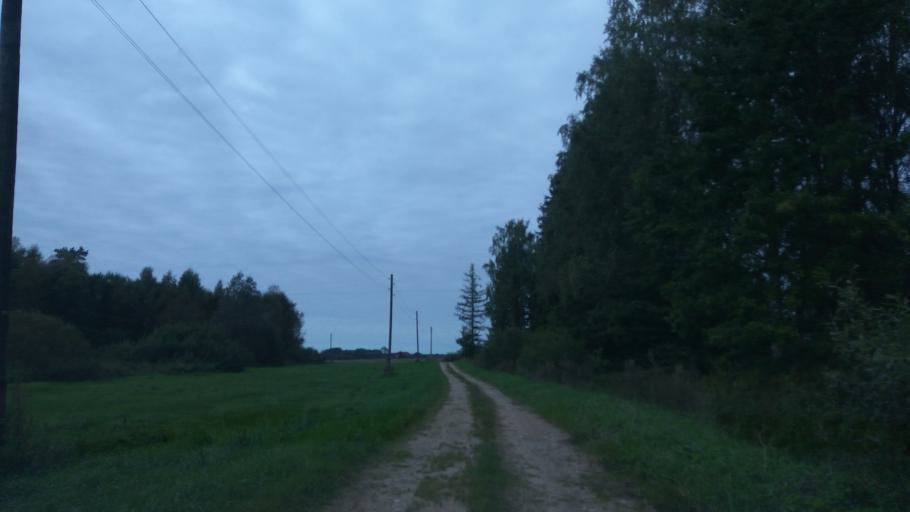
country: LV
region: Kuldigas Rajons
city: Kuldiga
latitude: 57.2411
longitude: 21.9631
